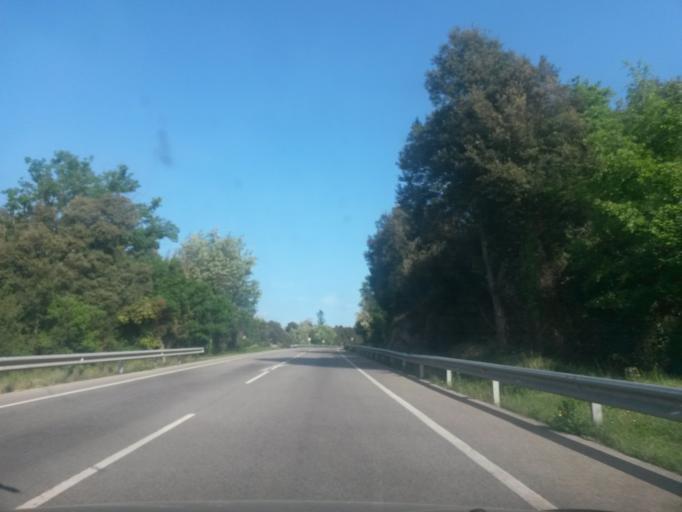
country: ES
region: Catalonia
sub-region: Provincia de Girona
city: les Planes d'Hostoles
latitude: 42.0673
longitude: 2.5271
